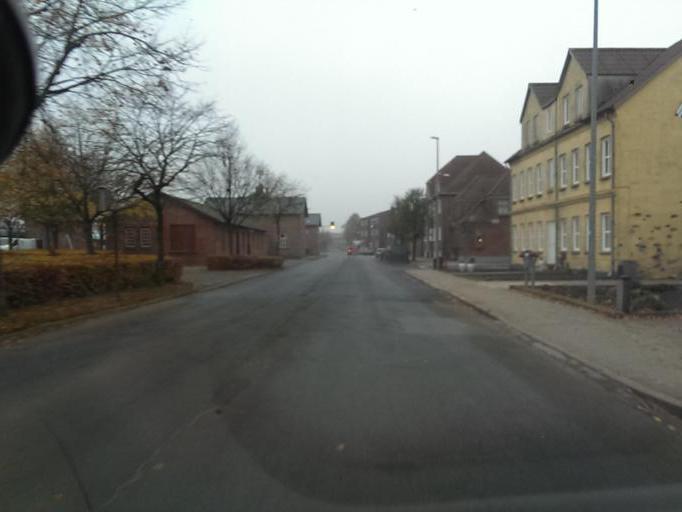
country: DK
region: South Denmark
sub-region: Esbjerg Kommune
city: Bramming
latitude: 55.4650
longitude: 8.7086
